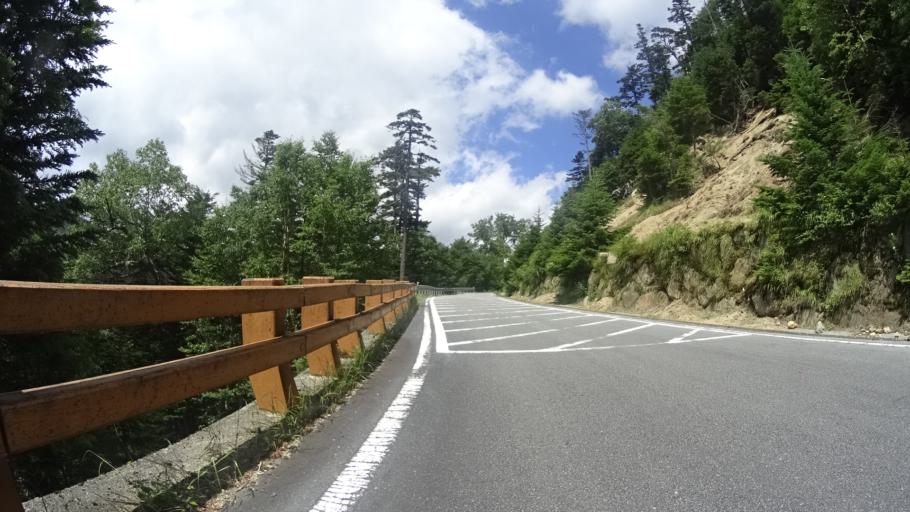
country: JP
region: Yamanashi
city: Enzan
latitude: 35.8659
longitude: 138.6623
